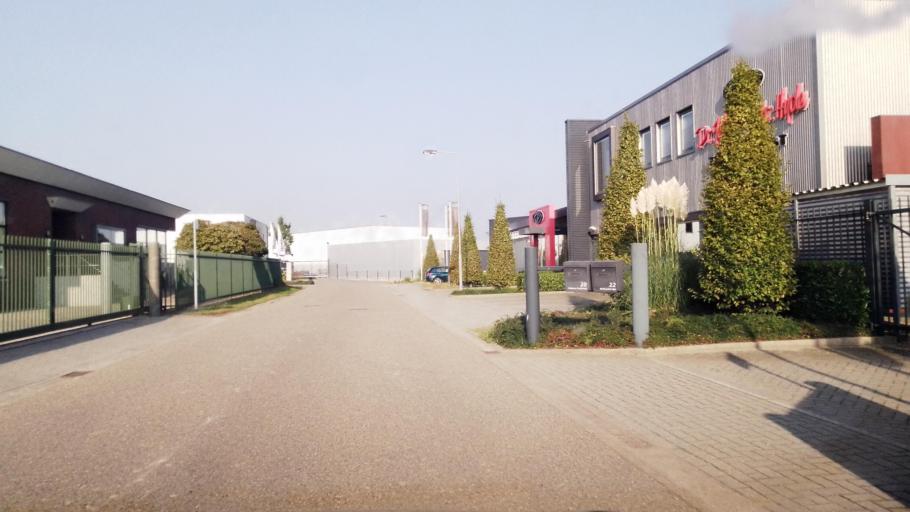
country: NL
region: Limburg
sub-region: Gemeente Venlo
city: Tegelen
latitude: 51.3179
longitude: 6.1201
